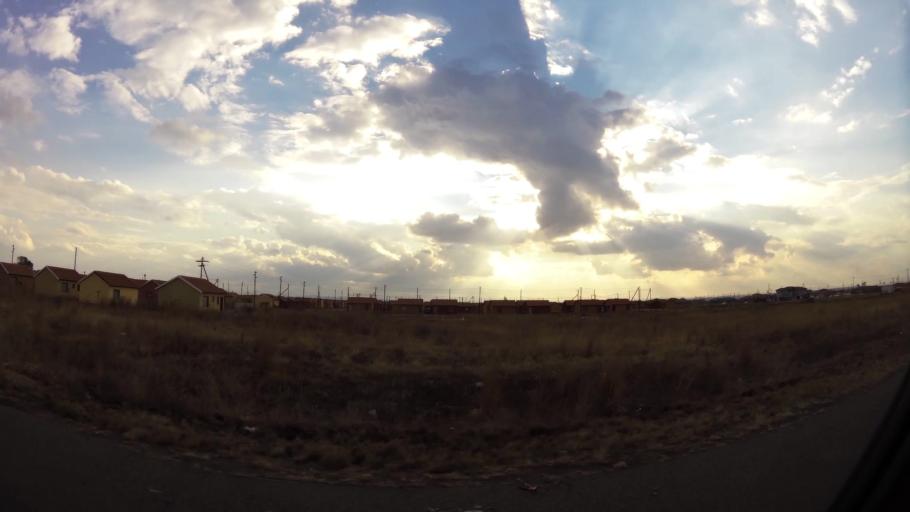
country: ZA
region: Gauteng
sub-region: Sedibeng District Municipality
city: Vanderbijlpark
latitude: -26.6156
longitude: 27.8135
